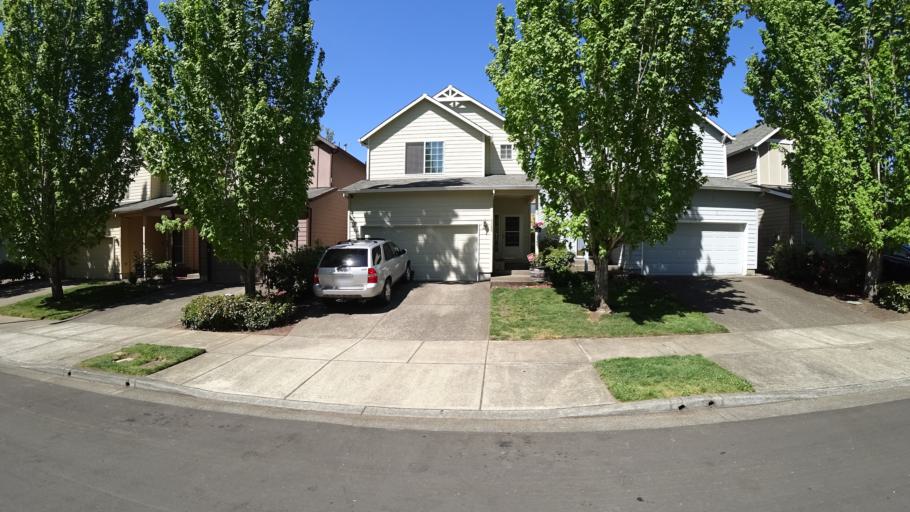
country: US
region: Oregon
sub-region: Washington County
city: Hillsboro
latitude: 45.5061
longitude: -122.9502
